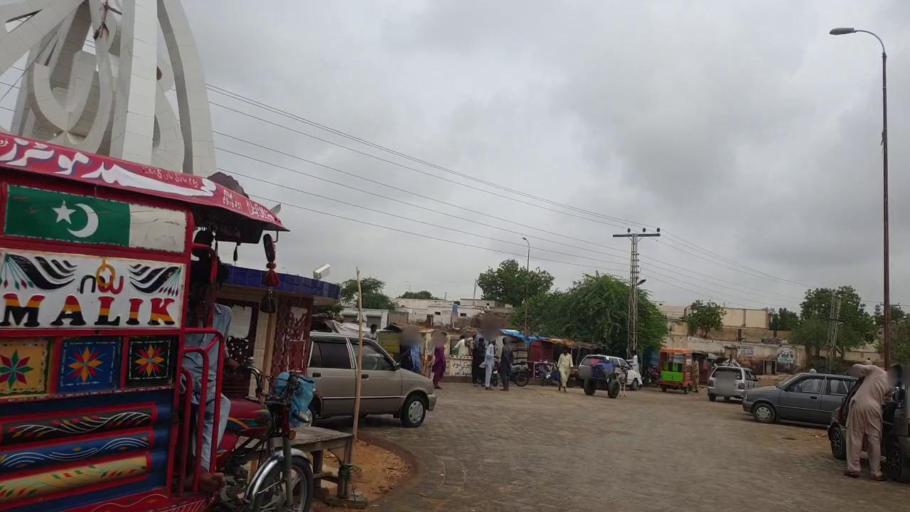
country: PK
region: Sindh
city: Diplo
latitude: 24.4691
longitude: 69.5795
